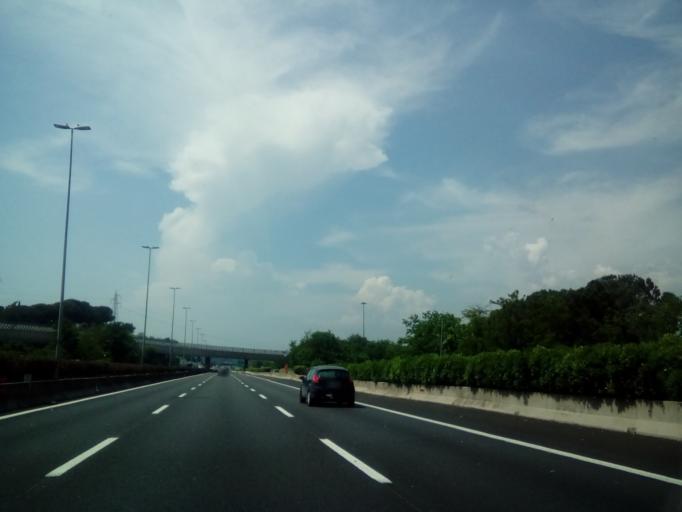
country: IT
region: Latium
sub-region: Citta metropolitana di Roma Capitale
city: Colle Verde
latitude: 41.9826
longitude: 12.5274
